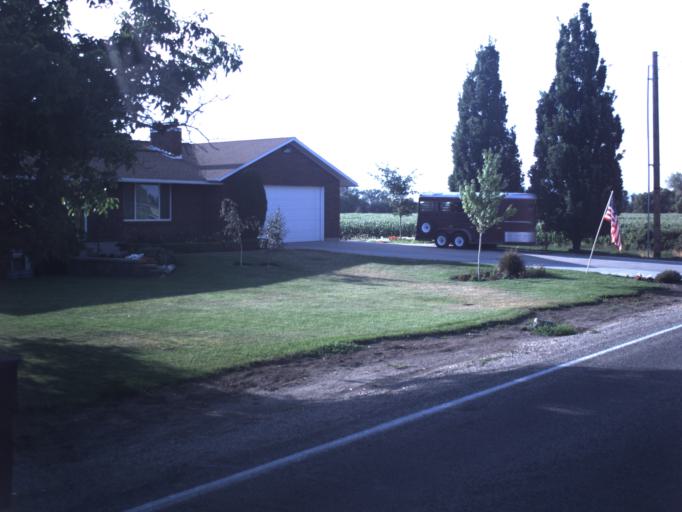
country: US
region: Utah
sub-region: Weber County
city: Plain City
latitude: 41.2818
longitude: -112.0932
